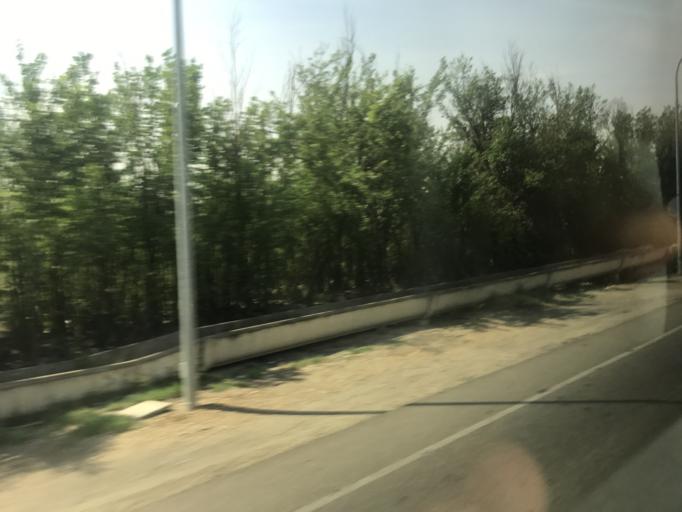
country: ES
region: Castille and Leon
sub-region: Provincia de Palencia
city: Palencia
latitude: 42.0160
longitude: -4.5156
